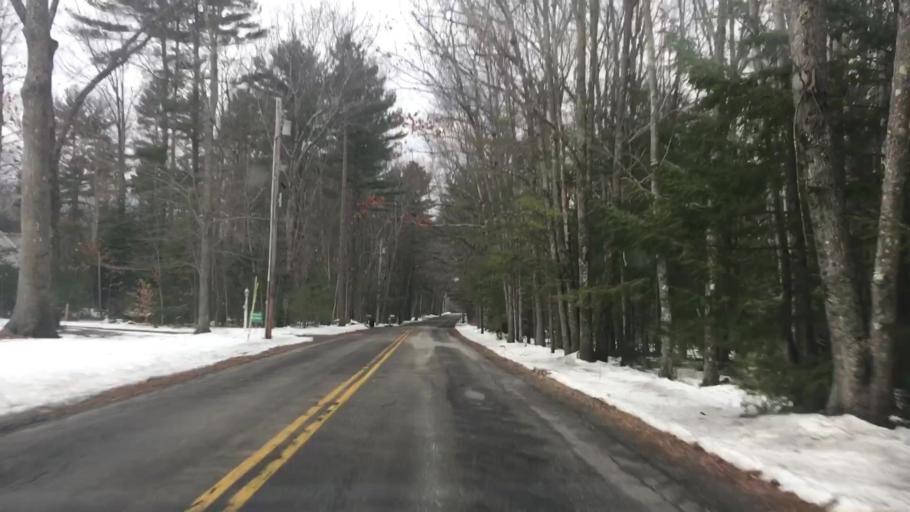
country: US
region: Maine
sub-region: York County
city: Wells Beach Station
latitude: 43.3413
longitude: -70.6106
